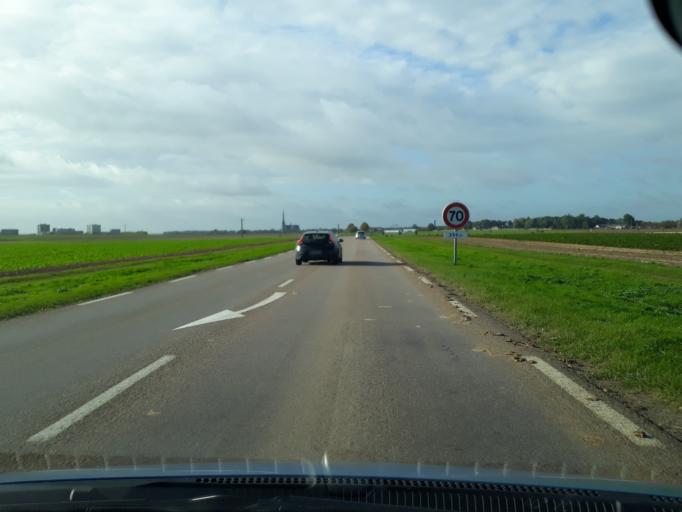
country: FR
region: Centre
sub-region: Departement du Loiret
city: Pithiviers
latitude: 48.1902
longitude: 2.2712
